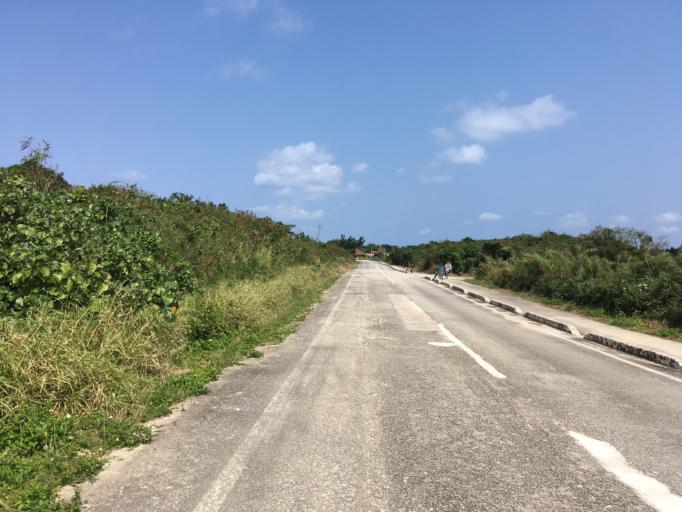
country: JP
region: Okinawa
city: Ishigaki
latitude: 24.3263
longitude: 124.0835
